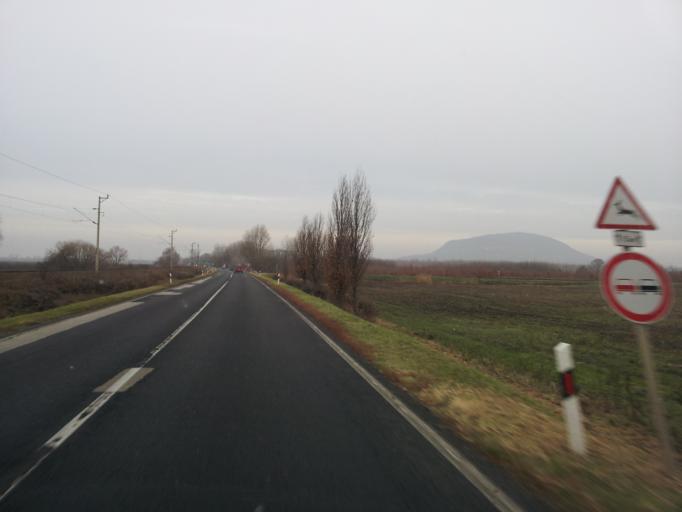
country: HU
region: Veszprem
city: Devecser
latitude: 47.1188
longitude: 17.4147
